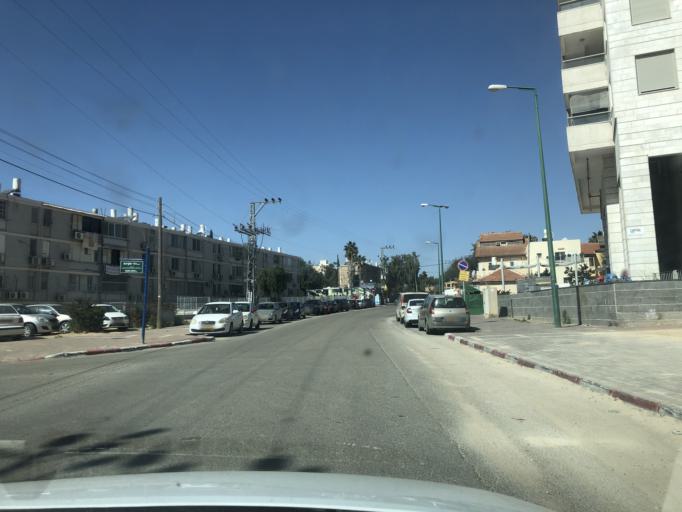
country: IL
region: Southern District
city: Beersheba
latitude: 31.2591
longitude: 34.7951
